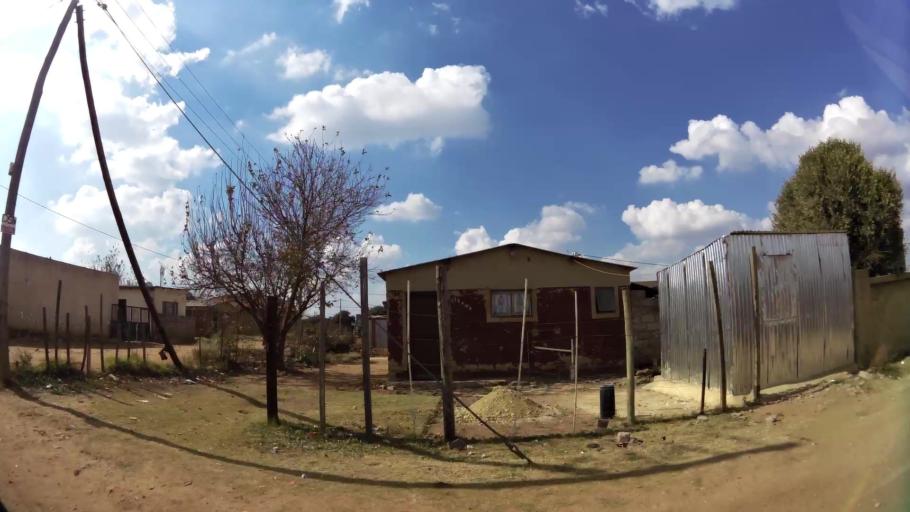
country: ZA
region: Gauteng
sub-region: City of Johannesburg Metropolitan Municipality
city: Roodepoort
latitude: -26.1950
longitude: 27.8707
